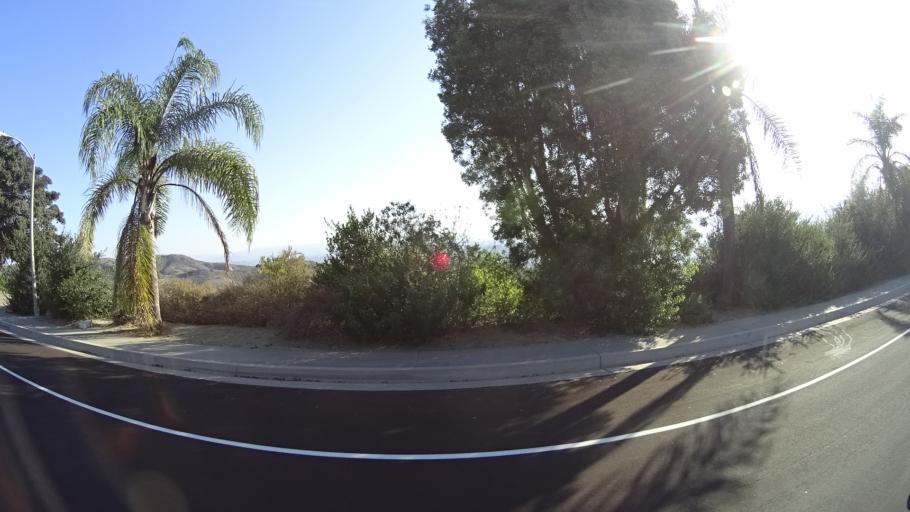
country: US
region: California
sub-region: Orange County
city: San Clemente
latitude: 33.4235
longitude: -117.5924
